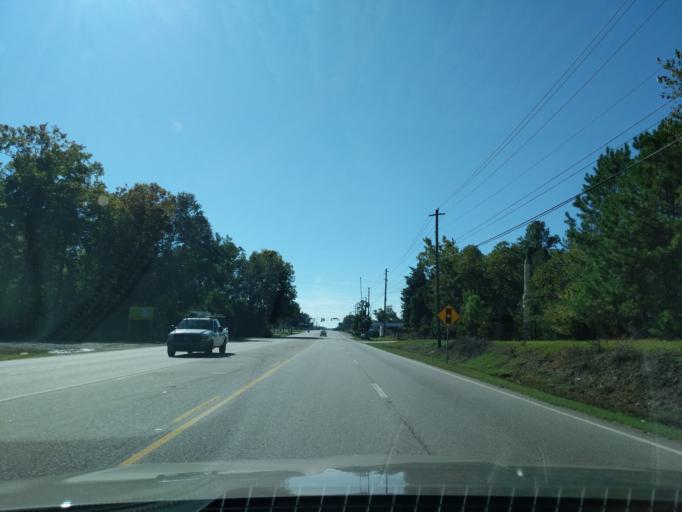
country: US
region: Georgia
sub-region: Richmond County
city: Augusta
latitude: 33.4190
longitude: -82.0072
